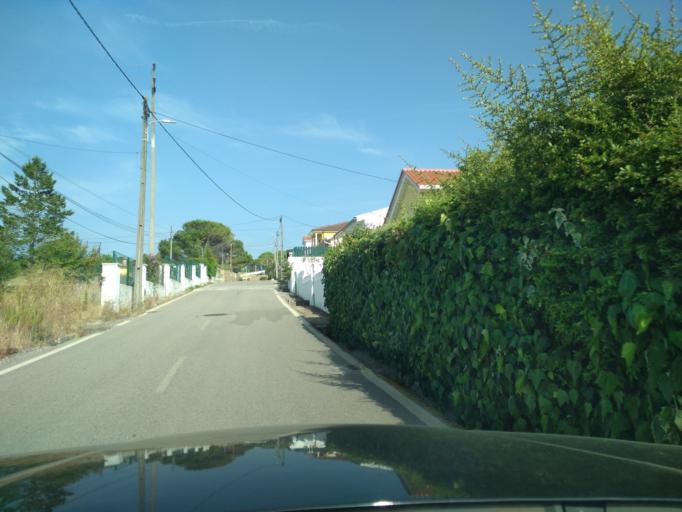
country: PT
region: Coimbra
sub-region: Condeixa-A-Nova
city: Condeixa-a-Nova
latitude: 40.1306
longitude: -8.4616
